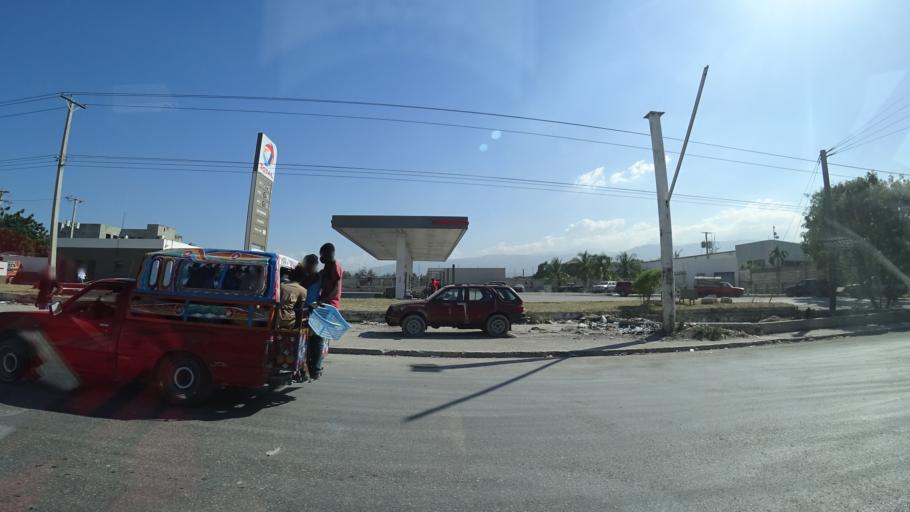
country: HT
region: Ouest
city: Delmas 73
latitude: 18.5788
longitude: -72.3148
